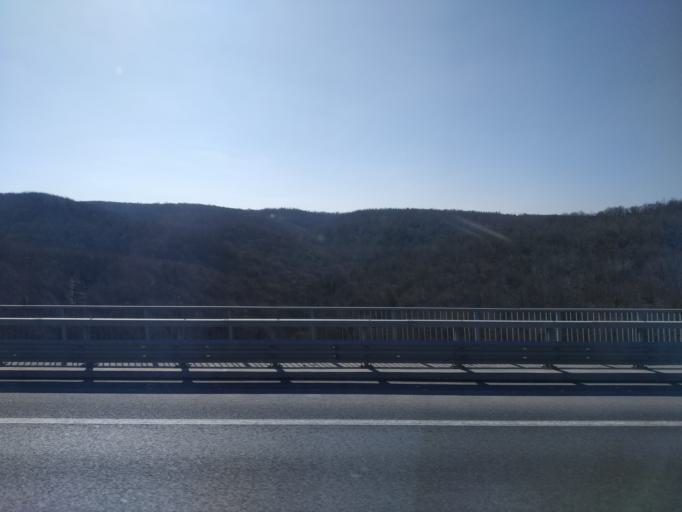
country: TR
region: Istanbul
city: Mahmut Sevket Pasa
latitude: 41.1695
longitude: 29.2493
